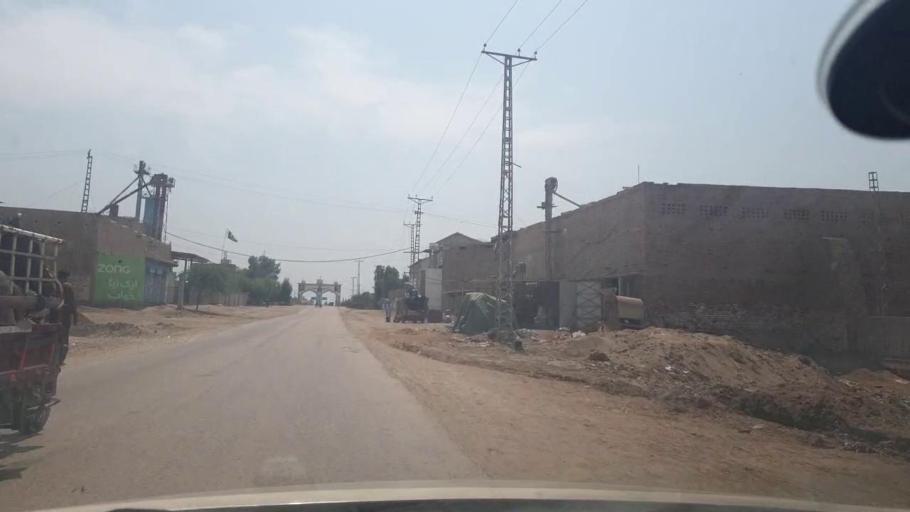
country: PK
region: Sindh
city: Jacobabad
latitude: 28.2452
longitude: 68.4664
